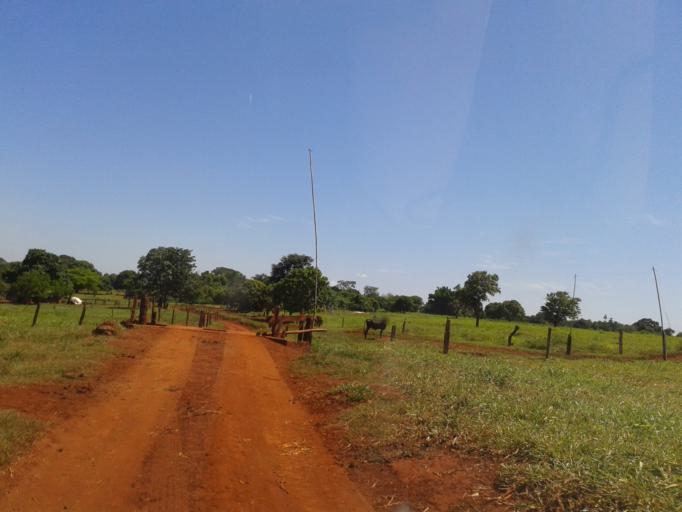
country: BR
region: Minas Gerais
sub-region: Centralina
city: Centralina
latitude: -18.6318
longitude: -49.2949
